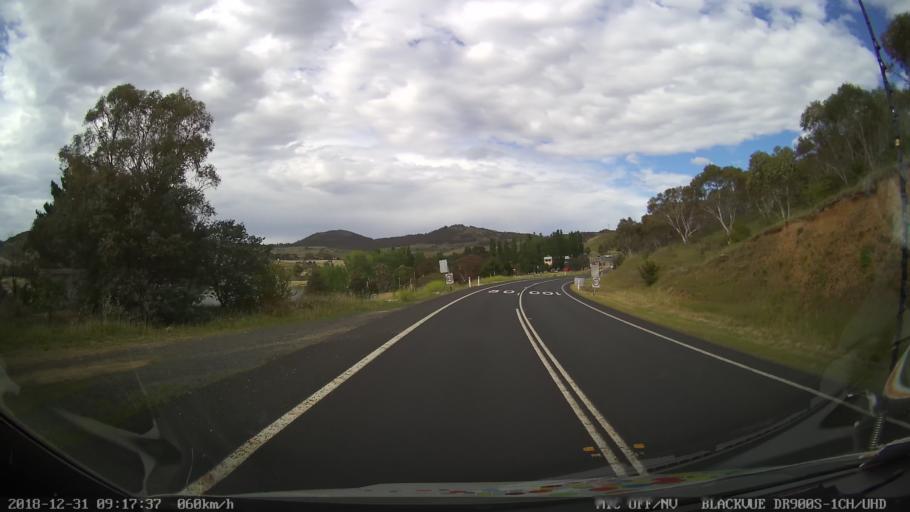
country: AU
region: New South Wales
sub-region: Snowy River
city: Jindabyne
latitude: -36.4076
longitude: 148.5998
